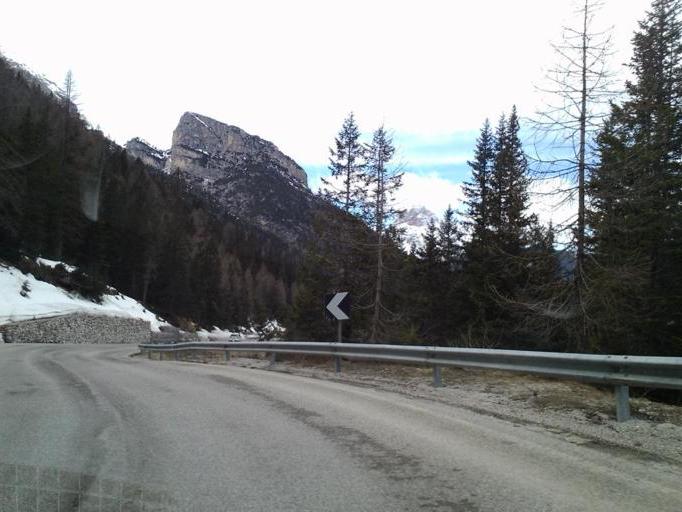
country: IT
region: Veneto
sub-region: Provincia di Belluno
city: Cortina d'Ampezzo
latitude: 46.5983
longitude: 12.2519
